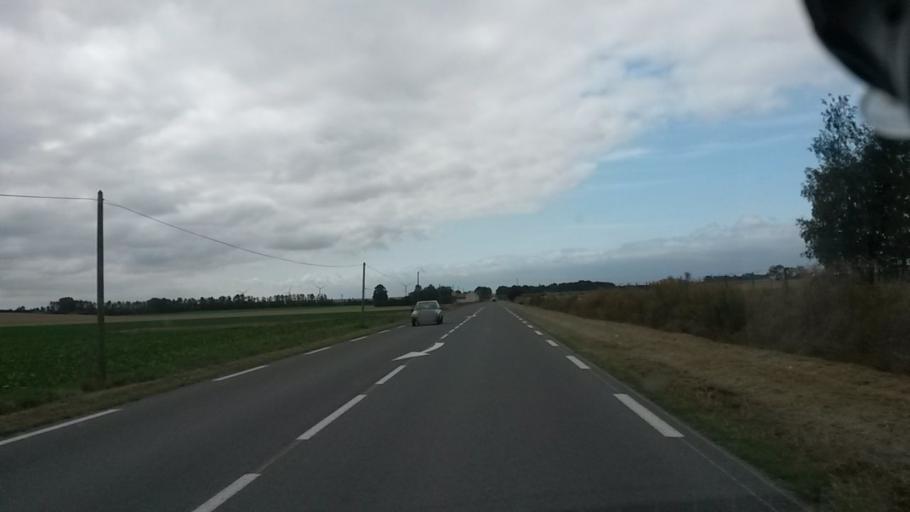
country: FR
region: Nord-Pas-de-Calais
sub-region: Departement du Pas-de-Calais
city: Bourlon
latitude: 50.1588
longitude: 3.1222
